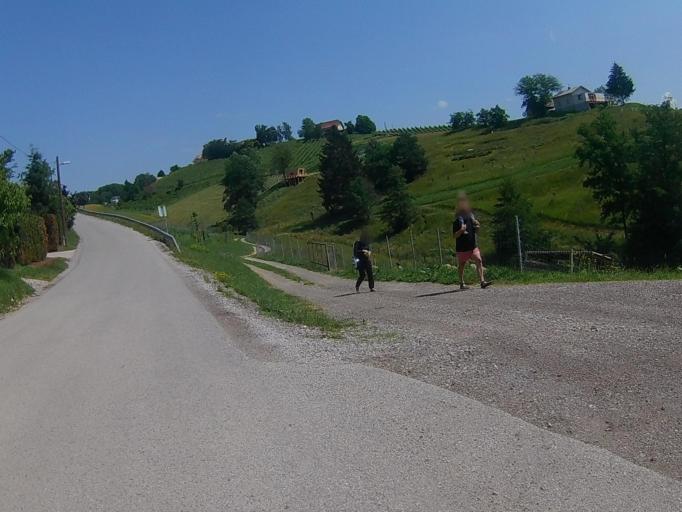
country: SI
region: Pesnica
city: Pesnica pri Mariboru
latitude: 46.5650
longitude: 15.6909
